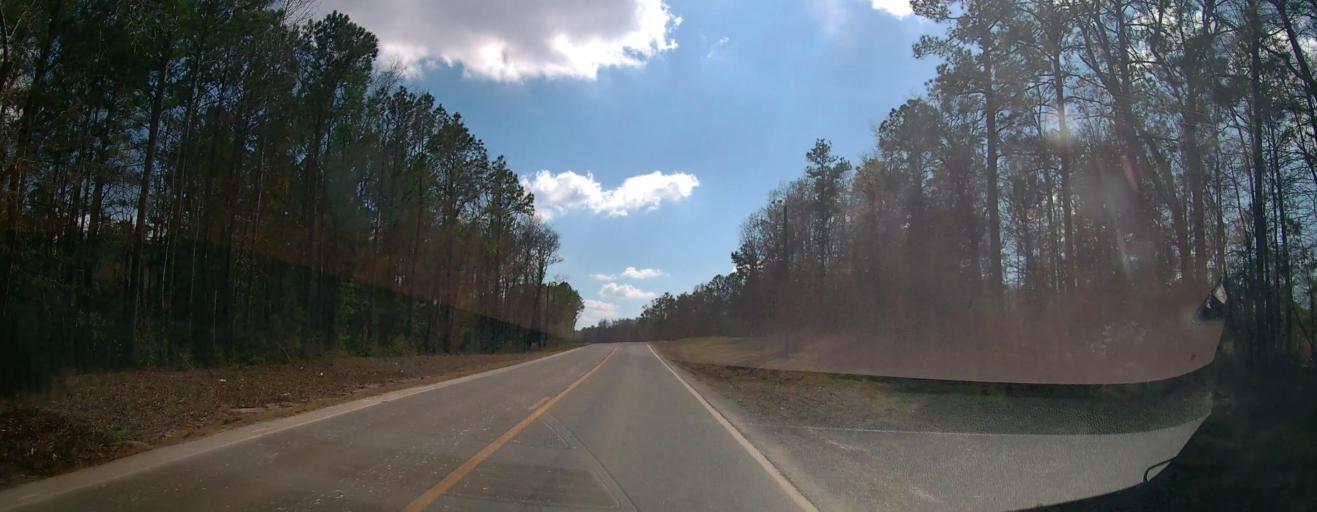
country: US
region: Georgia
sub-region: Wilkinson County
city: Gordon
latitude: 32.7982
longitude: -83.3301
